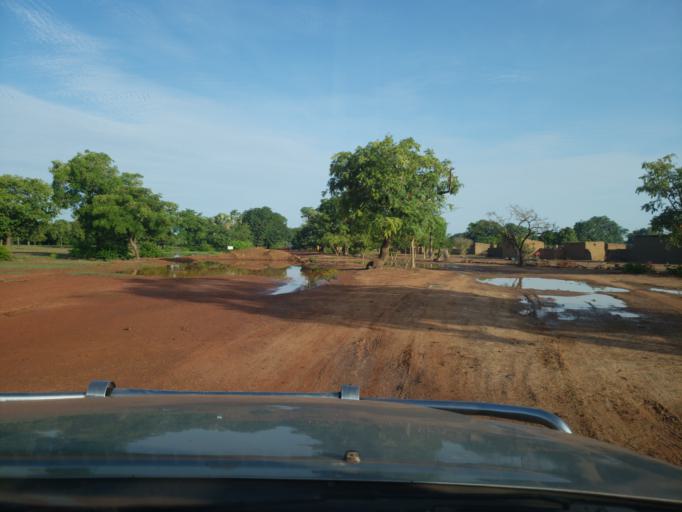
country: ML
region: Sikasso
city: Koutiala
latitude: 12.4208
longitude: -5.5828
